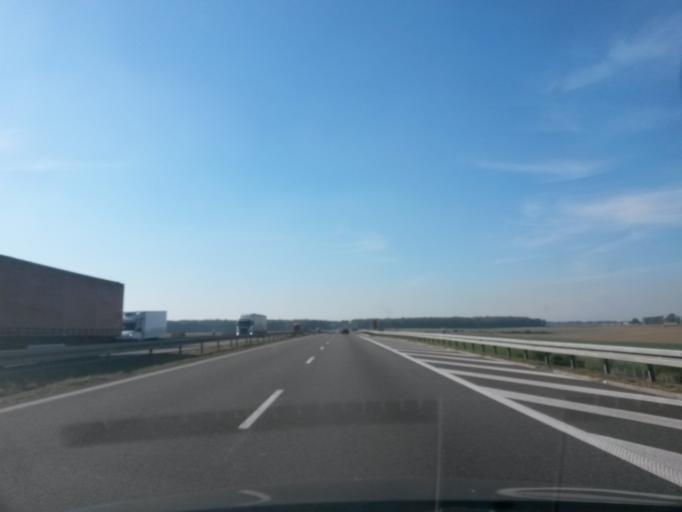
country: PL
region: Opole Voivodeship
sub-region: Powiat strzelecki
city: Strzelce Opolskie
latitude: 50.4498
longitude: 18.3235
